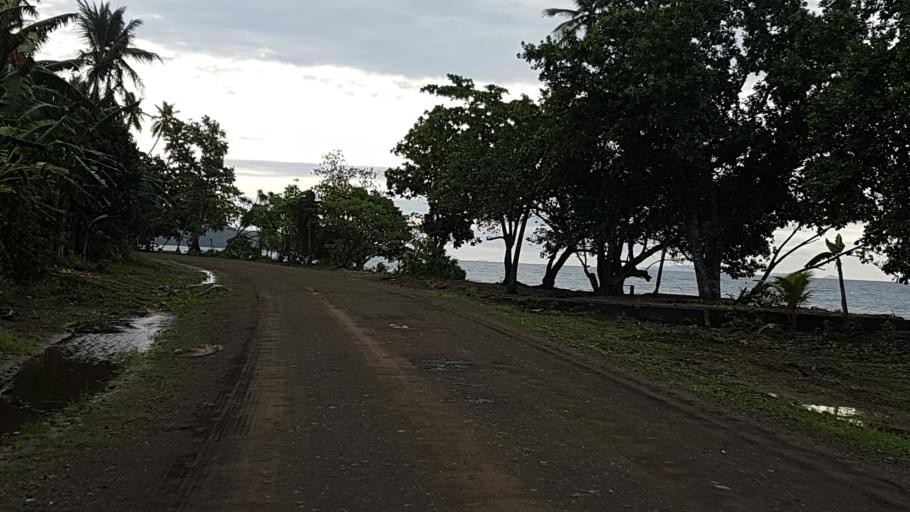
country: PG
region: Milne Bay
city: Alotau
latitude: -10.3156
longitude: 150.7175
